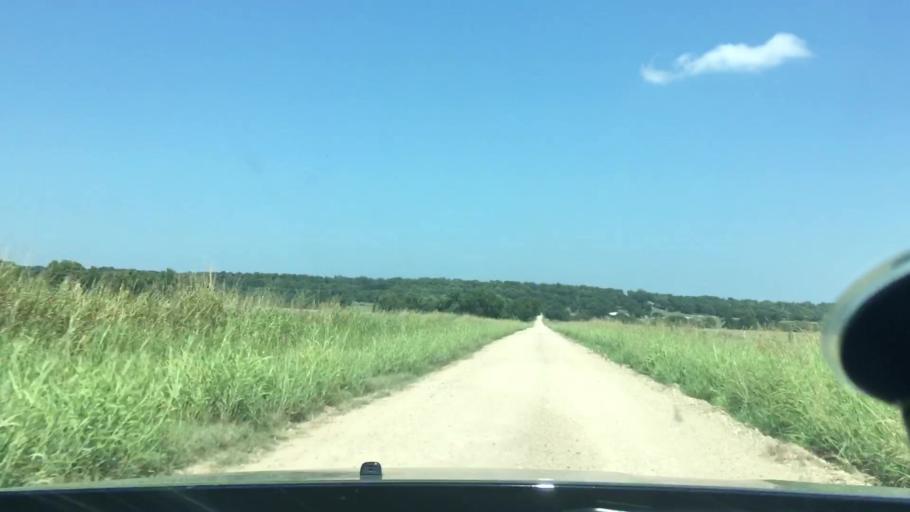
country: US
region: Oklahoma
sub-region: Johnston County
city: Tishomingo
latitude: 34.3532
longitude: -96.4420
